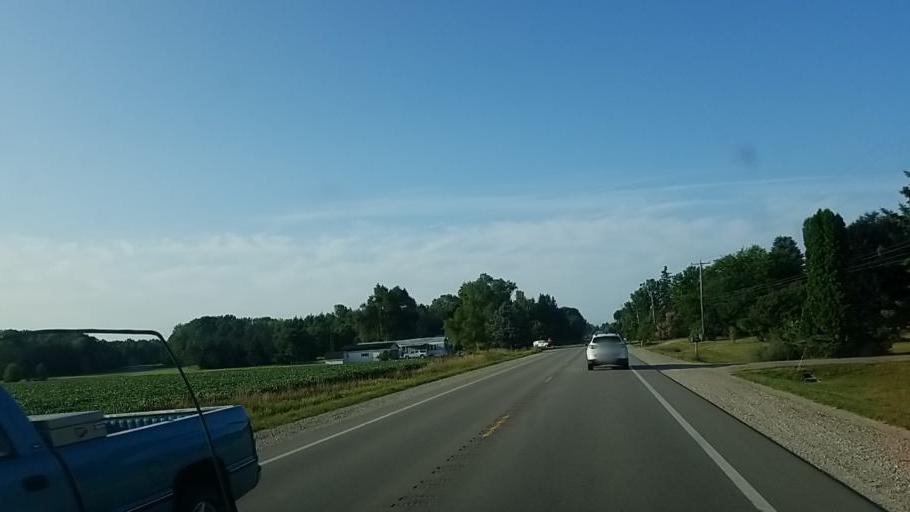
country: US
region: Michigan
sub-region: Montcalm County
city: Stanton
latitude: 43.2327
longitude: -85.0736
